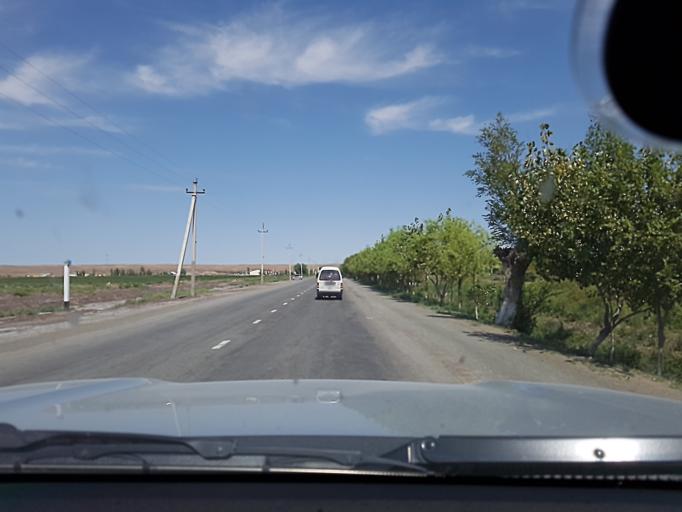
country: UZ
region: Karakalpakstan
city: Mang'it Shahri
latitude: 42.2387
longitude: 60.1433
